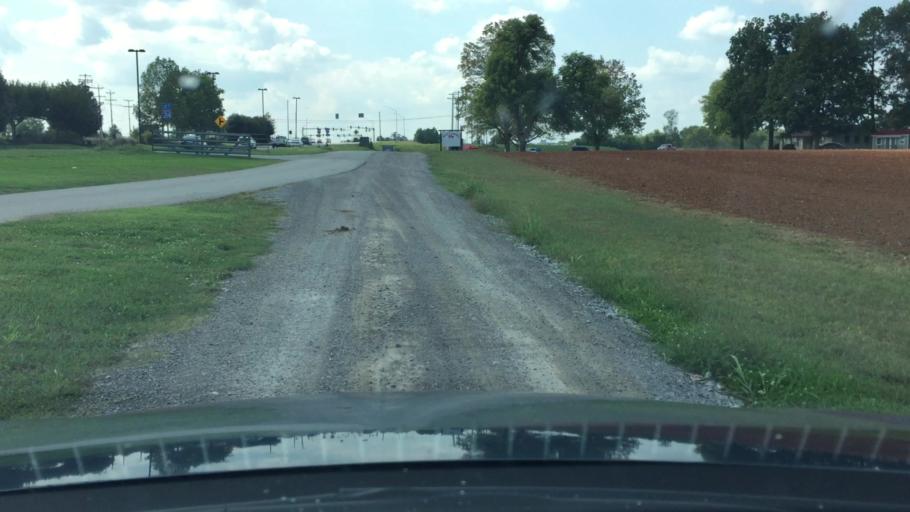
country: US
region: Tennessee
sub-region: Rutherford County
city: Murfreesboro
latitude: 35.8670
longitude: -86.4519
